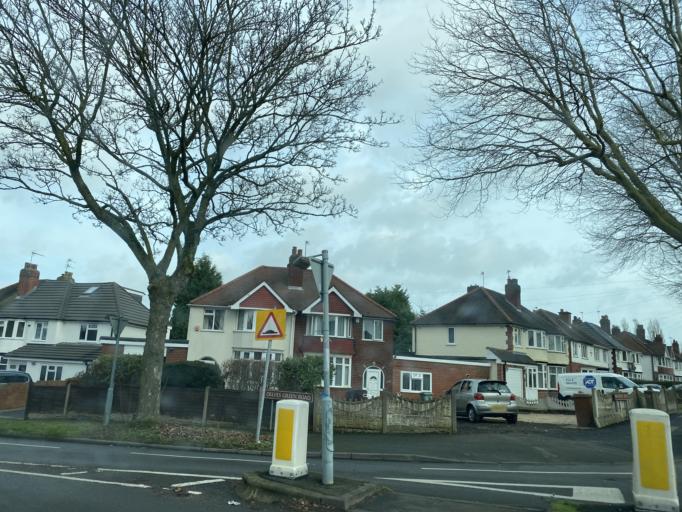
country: GB
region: England
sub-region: Walsall
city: Walsall
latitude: 52.5646
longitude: -1.9684
